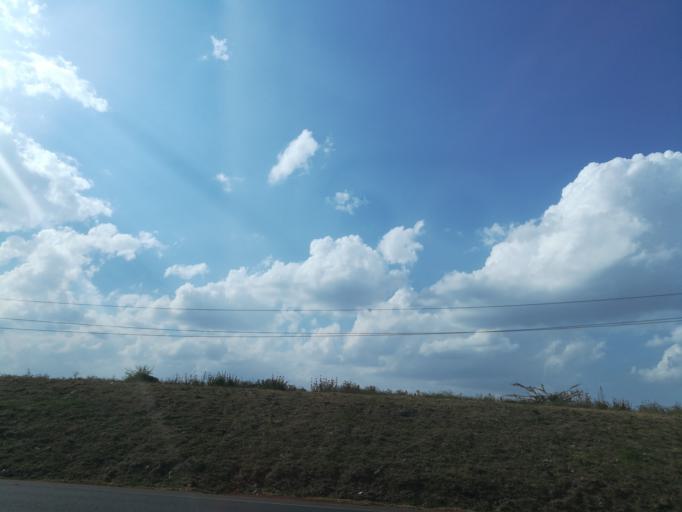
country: KE
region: Nairobi Area
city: Nairobi
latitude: -1.3329
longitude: 36.8078
